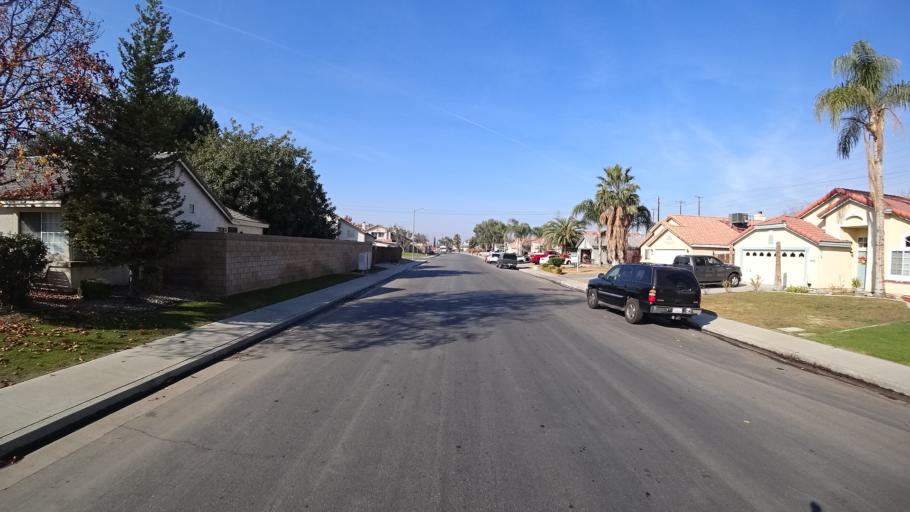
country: US
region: California
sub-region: Kern County
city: Greenfield
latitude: 35.3124
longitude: -119.0247
